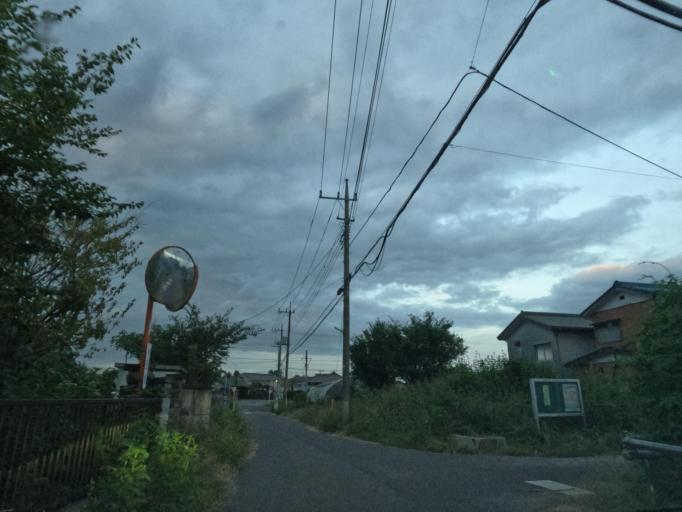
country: JP
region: Chiba
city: Noda
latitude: 35.9383
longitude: 139.8401
